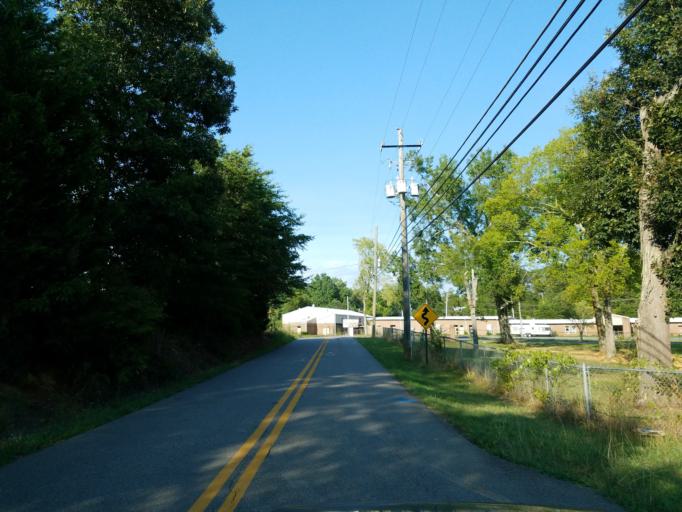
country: US
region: Georgia
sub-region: Bartow County
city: Rydal
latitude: 34.3427
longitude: -84.7329
